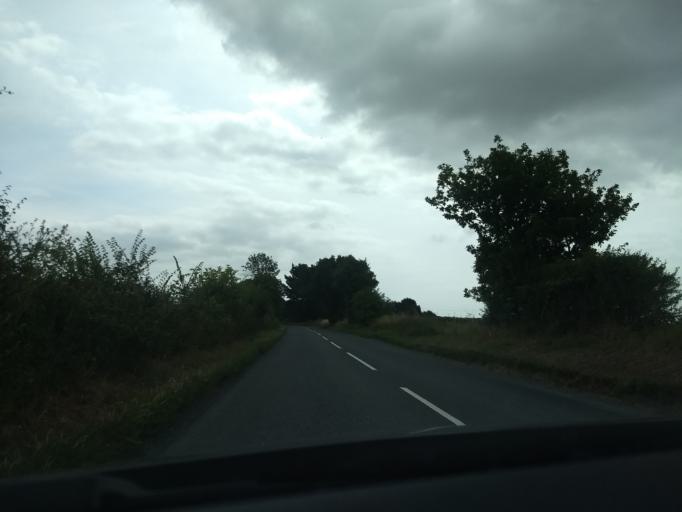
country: GB
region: England
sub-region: Suffolk
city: Ipswich
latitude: 51.9926
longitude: 1.1951
